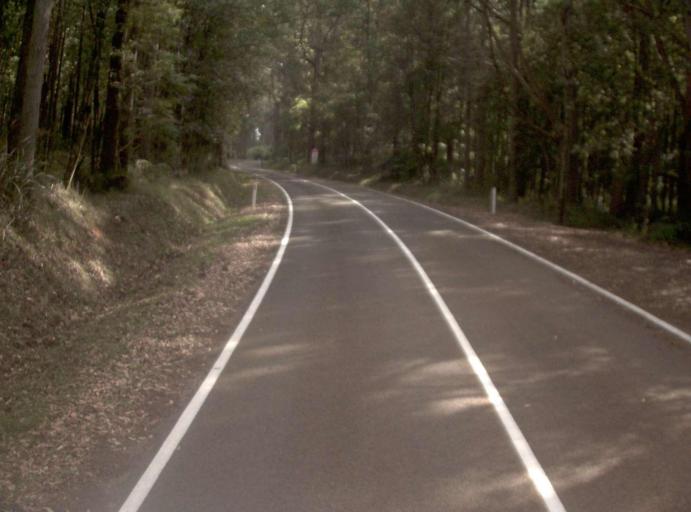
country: AU
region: Victoria
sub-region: Yarra Ranges
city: Badger Creek
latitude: -37.6981
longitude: 145.5753
